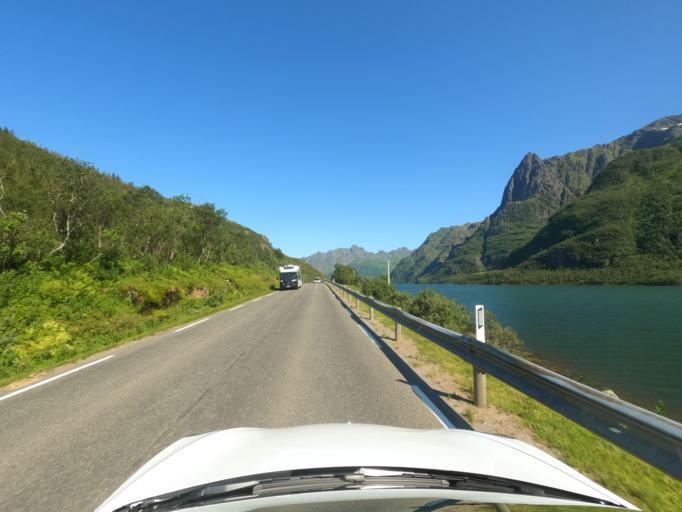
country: NO
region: Nordland
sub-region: Hadsel
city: Melbu
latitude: 68.3731
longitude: 14.7808
